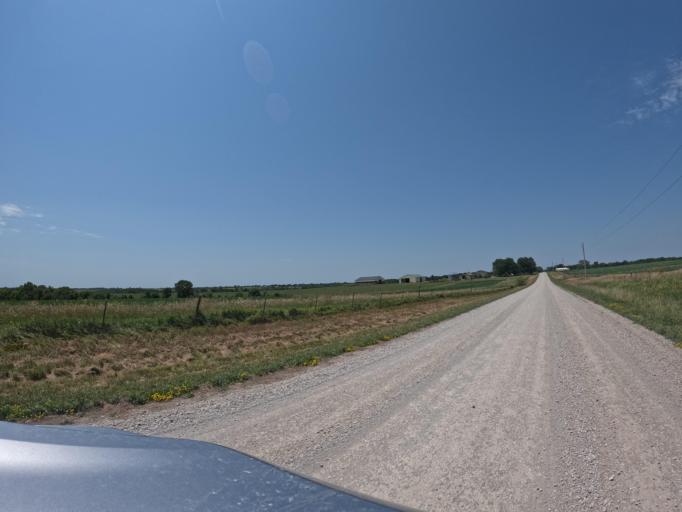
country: US
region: Iowa
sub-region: Appanoose County
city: Centerville
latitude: 40.7869
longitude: -92.9114
